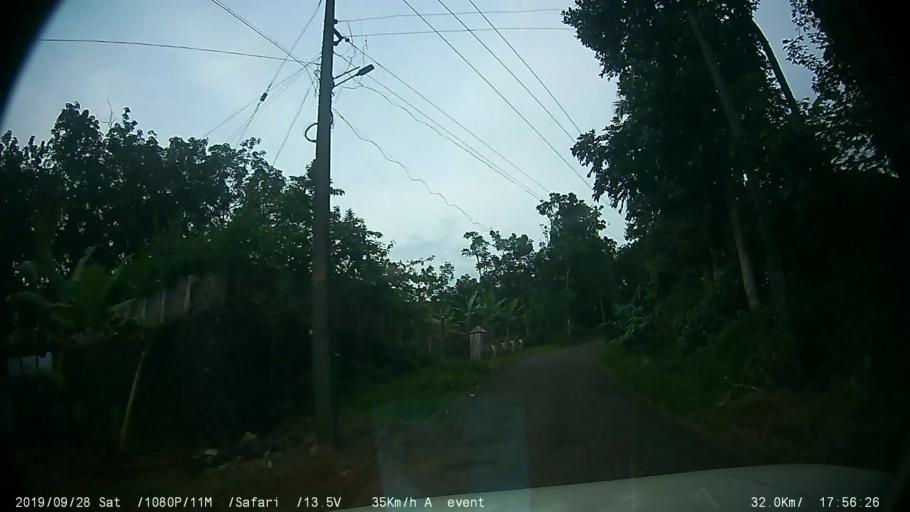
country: IN
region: Kerala
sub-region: Kottayam
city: Palackattumala
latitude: 9.7828
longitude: 76.5602
